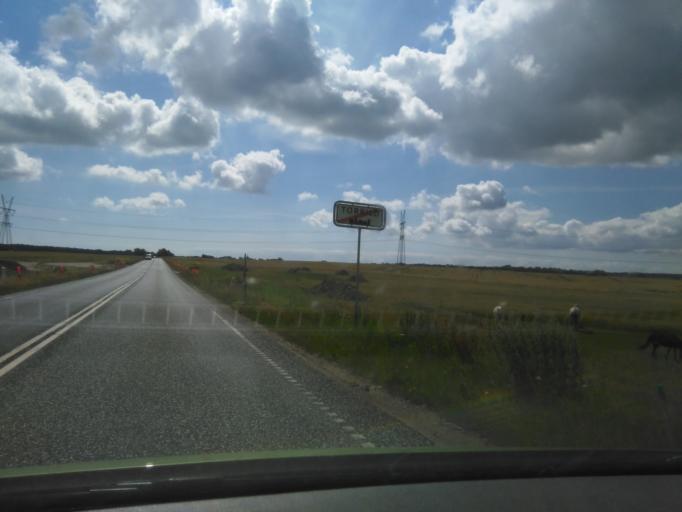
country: DK
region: Central Jutland
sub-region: Arhus Kommune
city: Solbjerg
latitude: 55.9775
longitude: 10.0529
